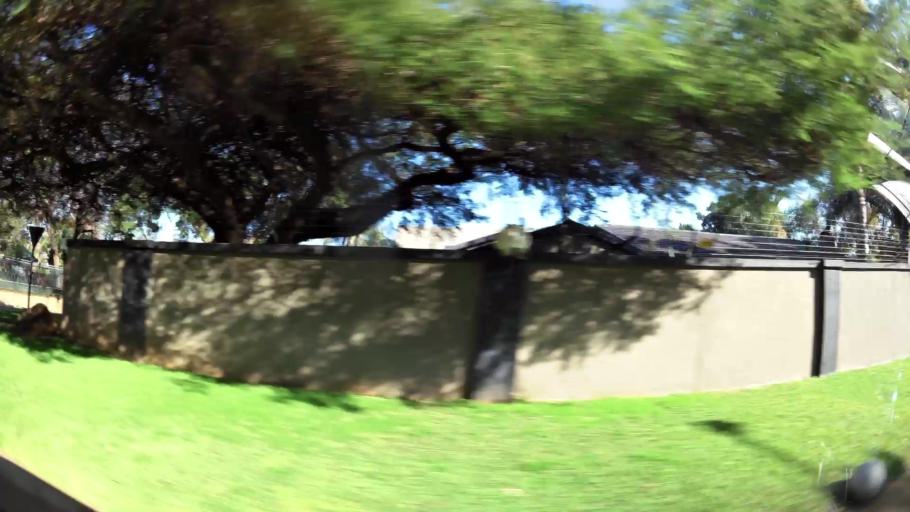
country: ZA
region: Gauteng
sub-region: City of Tshwane Metropolitan Municipality
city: Pretoria
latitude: -25.6688
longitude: 28.2340
